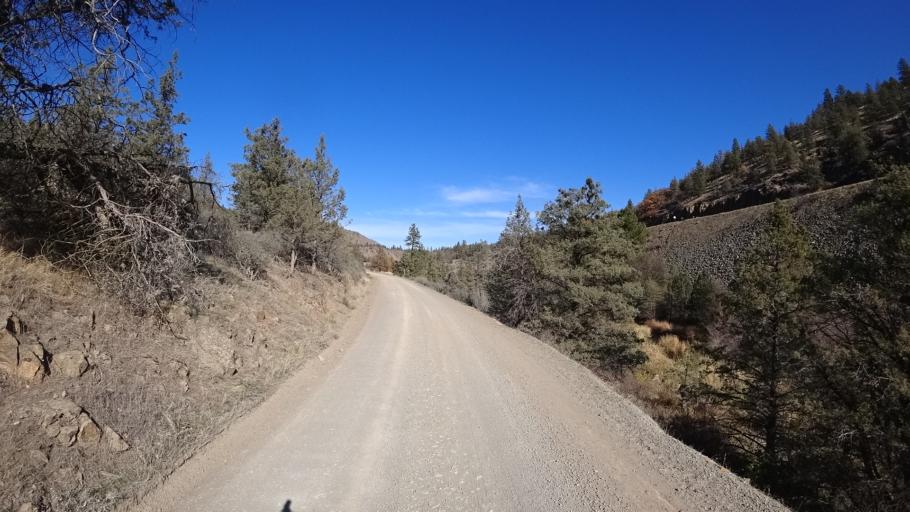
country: US
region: California
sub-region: Siskiyou County
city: Yreka
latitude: 41.7962
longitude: -122.6057
